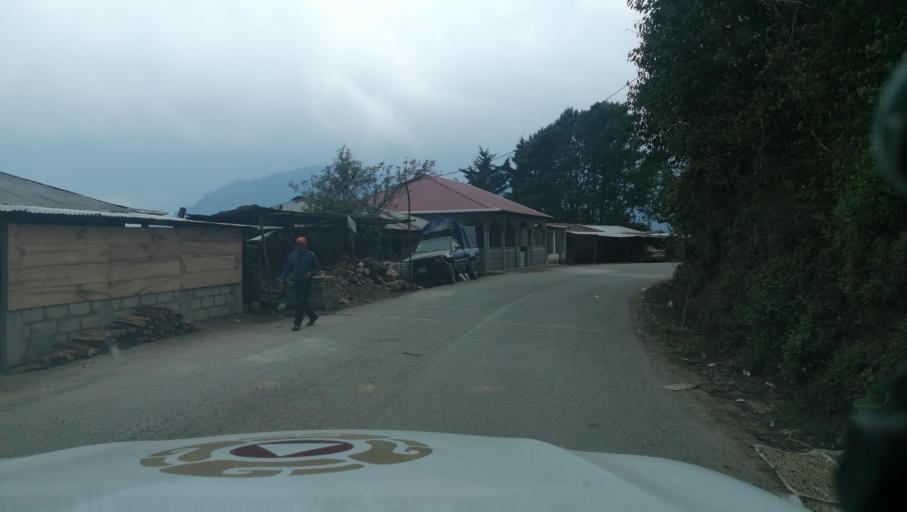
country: GT
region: San Marcos
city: Tacana
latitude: 15.2039
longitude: -92.1845
